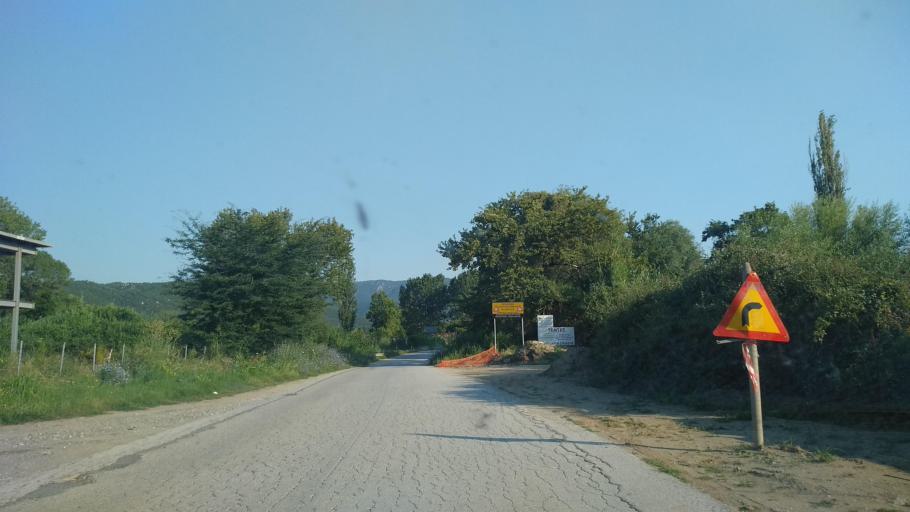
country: GR
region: Central Macedonia
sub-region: Nomos Thessalonikis
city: Stavros
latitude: 40.6749
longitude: 23.6887
